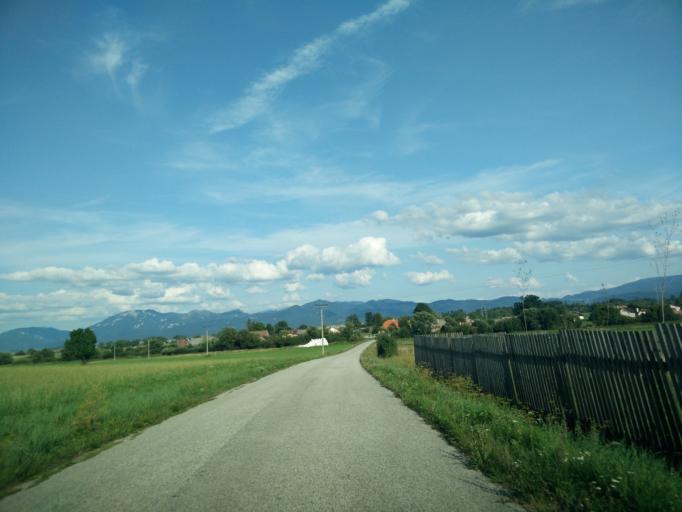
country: SK
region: Nitriansky
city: Handlova
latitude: 48.8899
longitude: 18.7706
